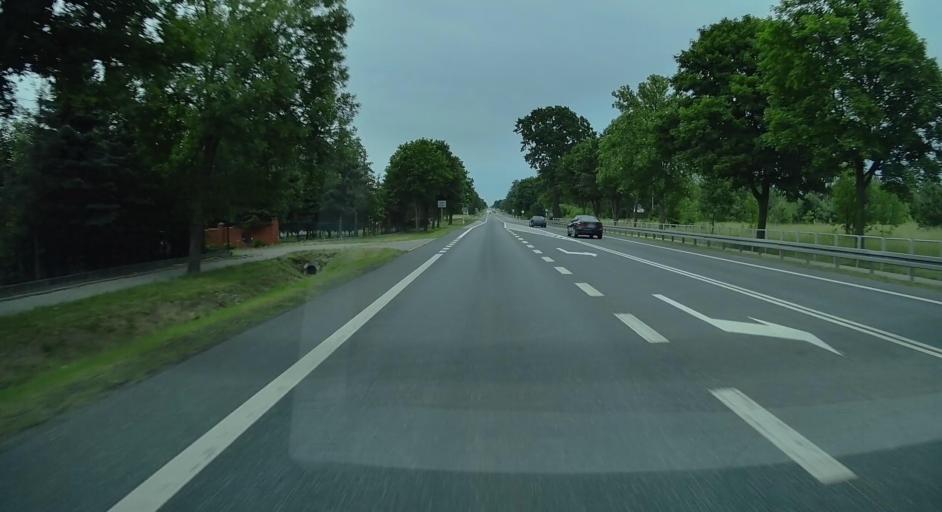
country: PL
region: Lublin Voivodeship
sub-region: Powiat bialski
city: Zalesie
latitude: 52.0347
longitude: 23.3083
